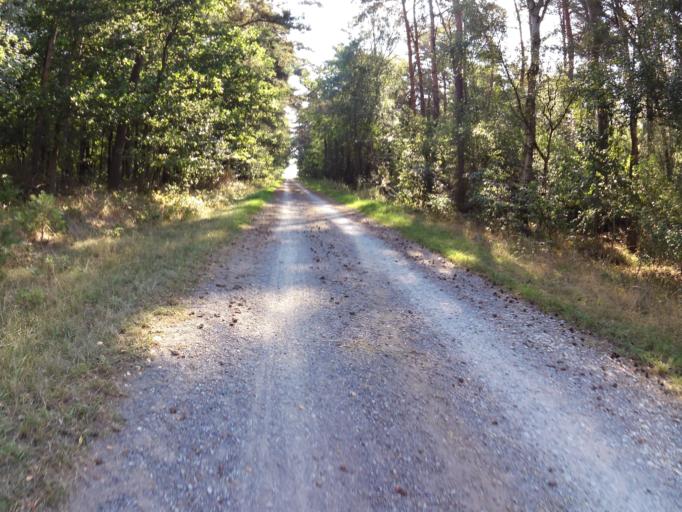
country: DE
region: North Rhine-Westphalia
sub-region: Regierungsbezirk Munster
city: Beelen
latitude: 51.9511
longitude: 8.1550
